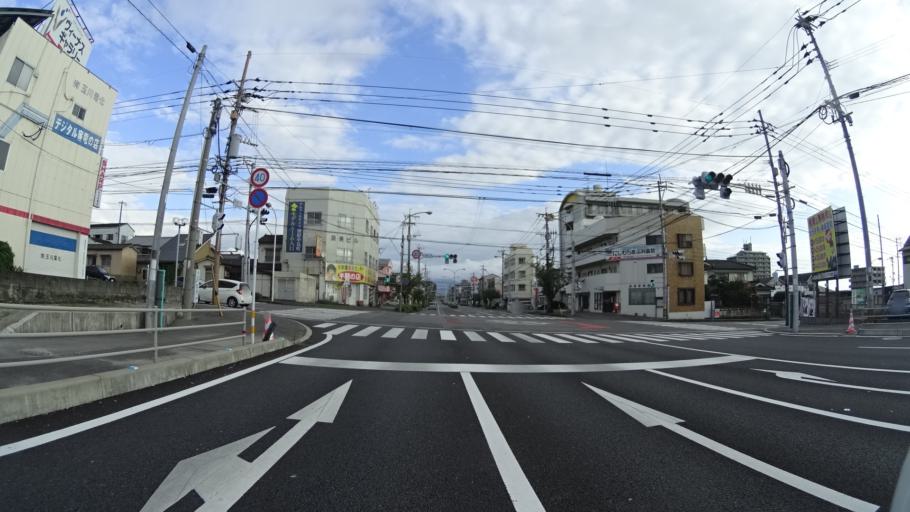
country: JP
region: Oita
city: Beppu
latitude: 33.2842
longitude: 131.4967
